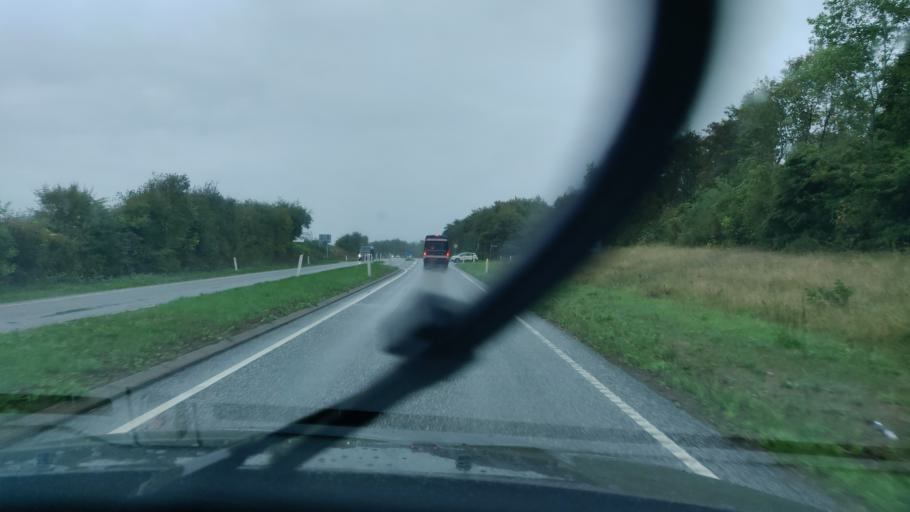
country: DK
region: North Denmark
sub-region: Thisted Kommune
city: Thisted
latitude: 56.9709
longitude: 8.7127
